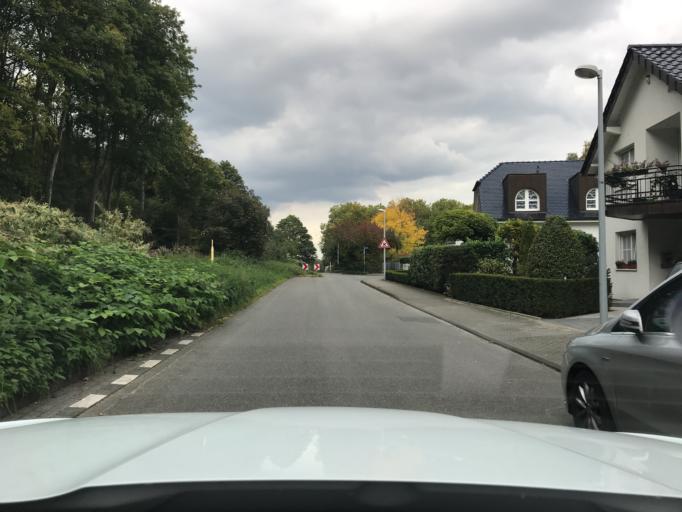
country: DE
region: North Rhine-Westphalia
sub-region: Regierungsbezirk Dusseldorf
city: Duisburg
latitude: 51.4368
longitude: 6.8181
